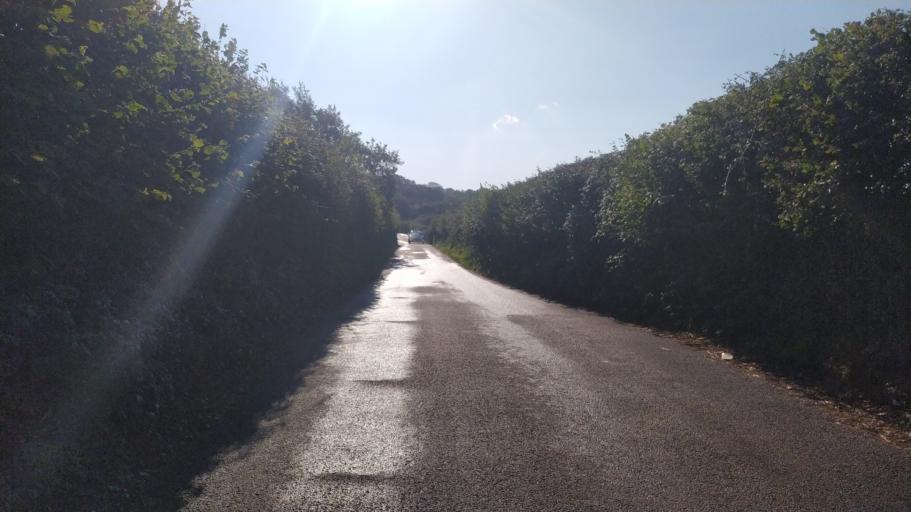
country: GB
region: England
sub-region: Isle of Wight
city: Newport
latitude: 50.6910
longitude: -1.3460
